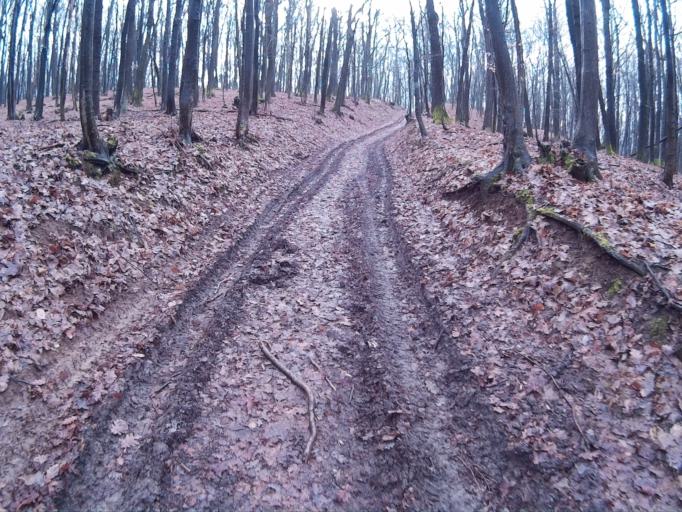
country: HU
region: Borsod-Abauj-Zemplen
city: Satoraljaujhely
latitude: 48.4171
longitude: 21.5839
